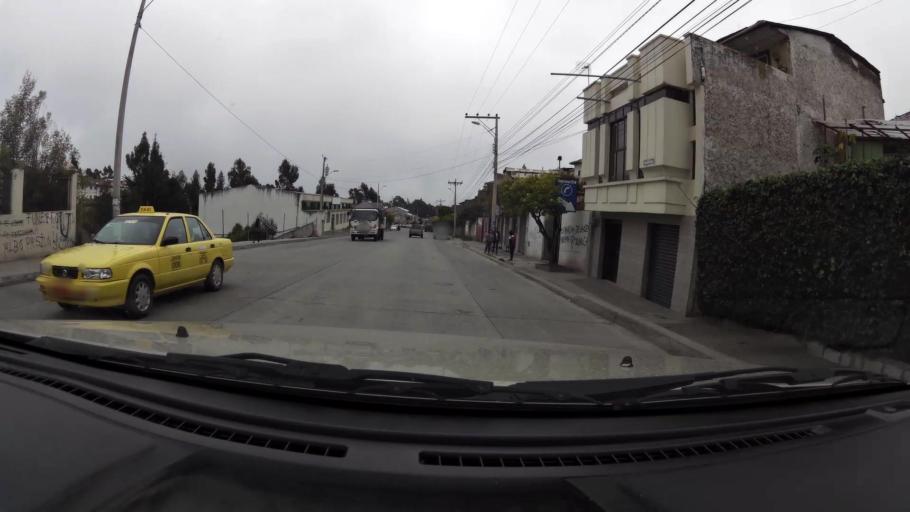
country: EC
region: Canar
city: Canar
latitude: -2.5555
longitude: -78.9413
